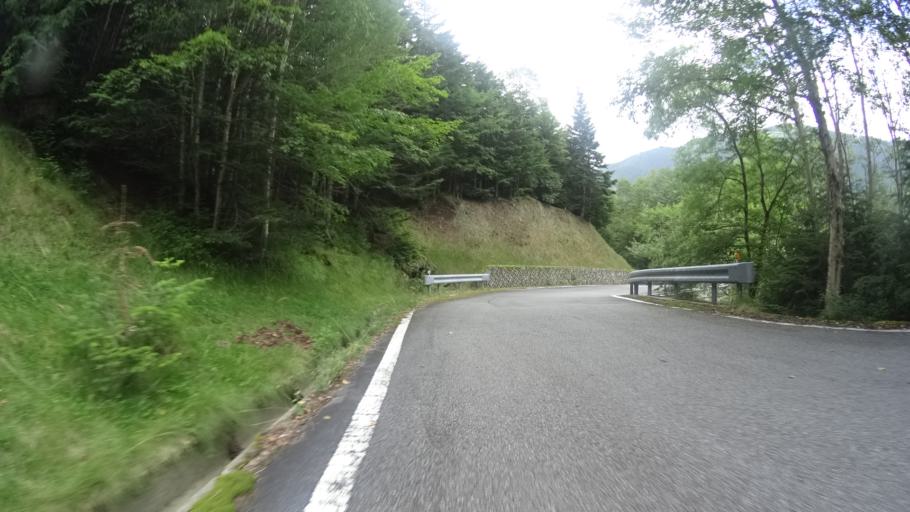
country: JP
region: Yamanashi
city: Enzan
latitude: 35.8592
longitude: 138.6569
